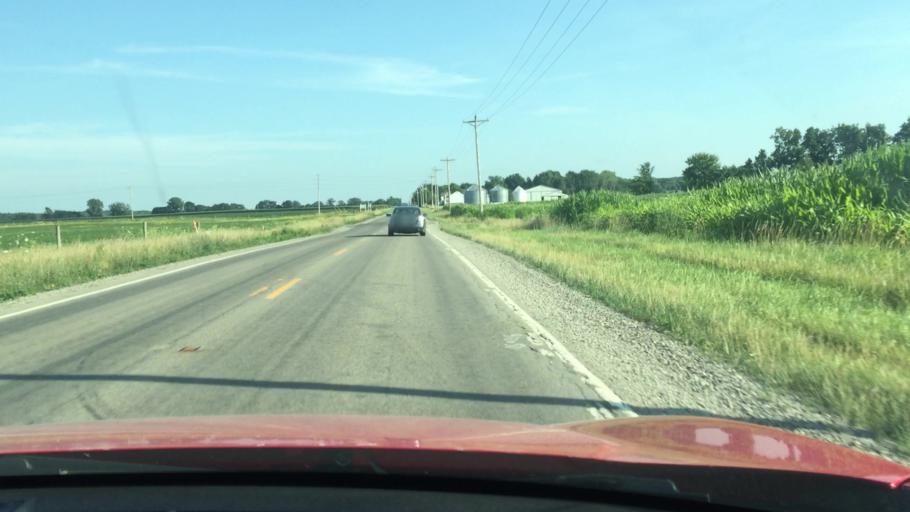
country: US
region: Ohio
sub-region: Hardin County
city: Ada
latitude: 40.6621
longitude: -83.8519
